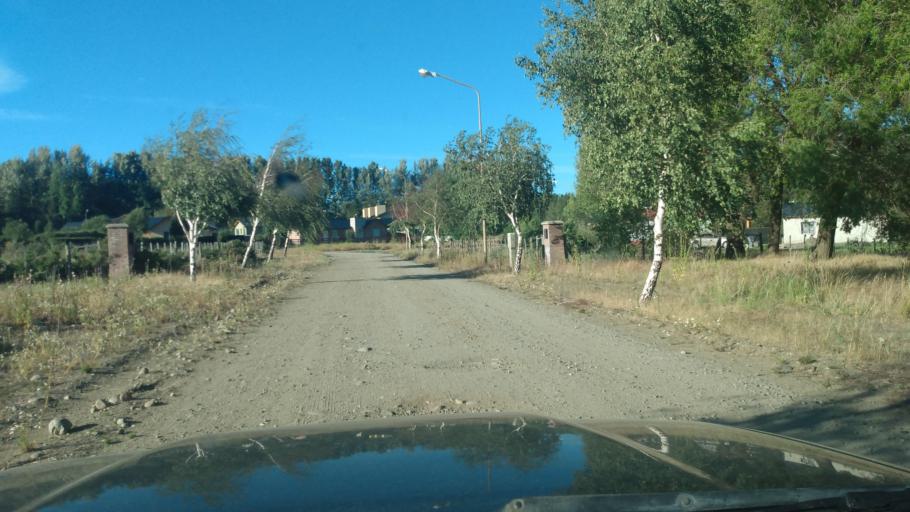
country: AR
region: Neuquen
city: Junin de los Andes
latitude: -39.9649
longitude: -71.0818
